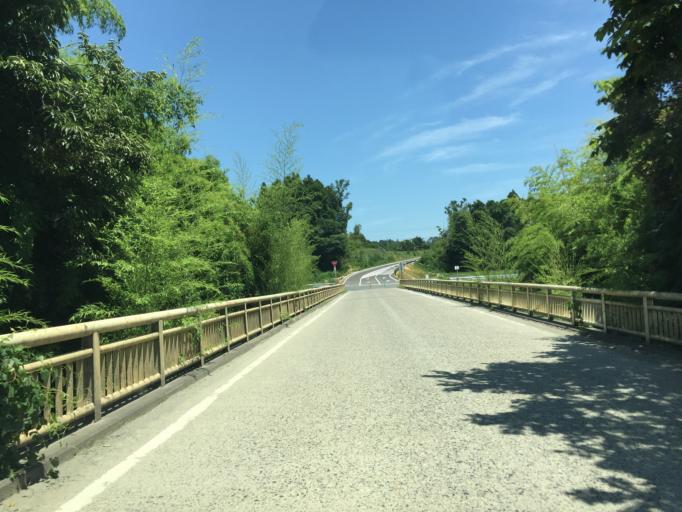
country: JP
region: Miyagi
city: Marumori
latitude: 37.7761
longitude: 140.8875
